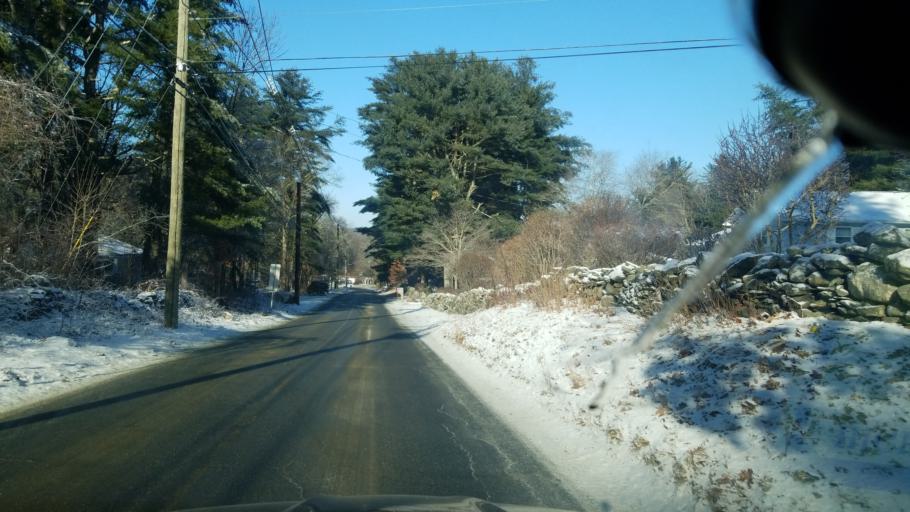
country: US
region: Connecticut
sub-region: Windham County
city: East Brooklyn
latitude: 41.8108
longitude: -71.9067
